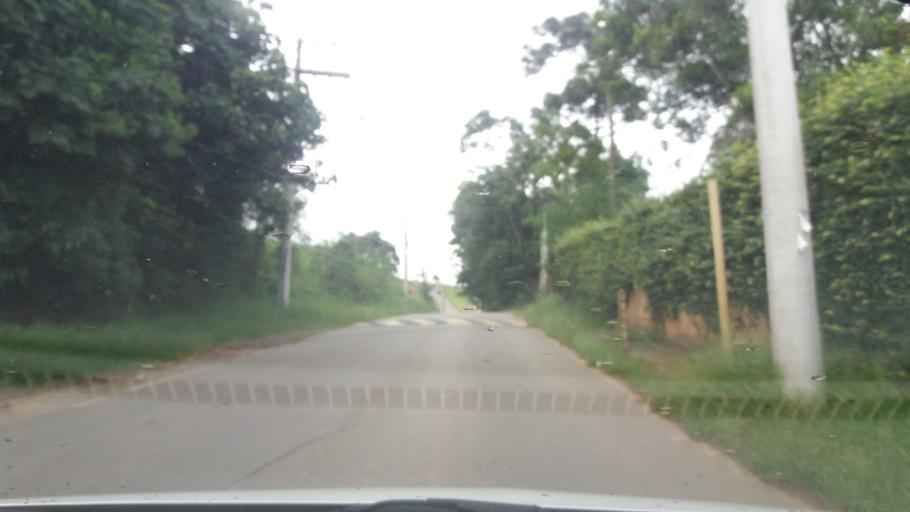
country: BR
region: Sao Paulo
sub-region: Bom Jesus Dos Perdoes
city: Bom Jesus dos Perdoes
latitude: -23.1725
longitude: -46.4374
